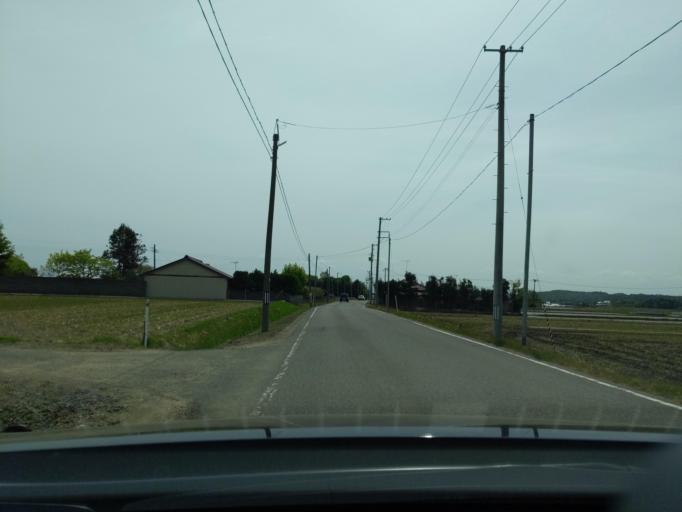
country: JP
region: Fukushima
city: Koriyama
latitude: 37.4044
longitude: 140.2588
